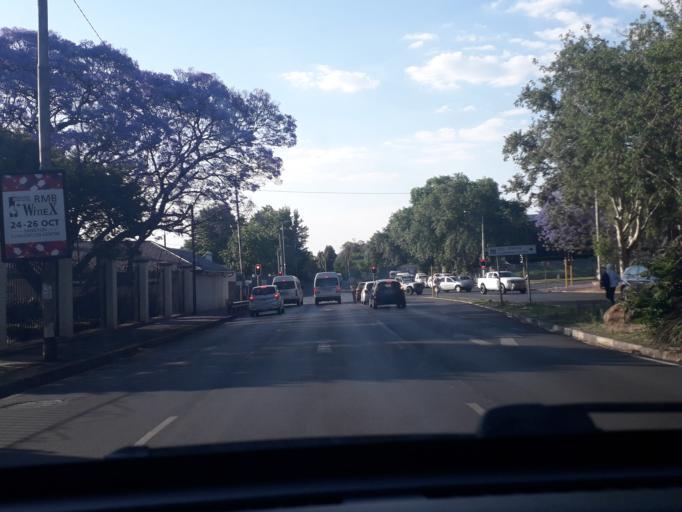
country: ZA
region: Gauteng
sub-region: City of Johannesburg Metropolitan Municipality
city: Johannesburg
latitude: -26.1819
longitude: 28.0305
